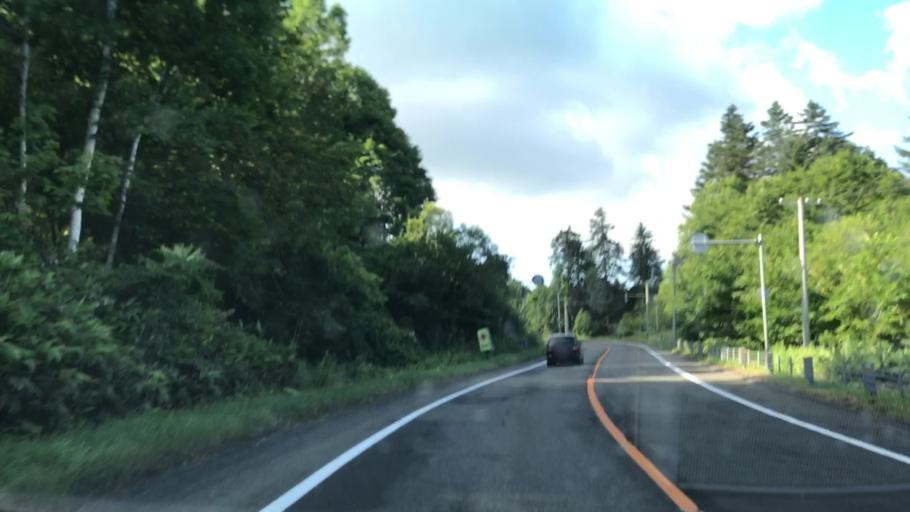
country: JP
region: Hokkaido
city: Shimo-furano
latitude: 42.9109
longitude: 142.4111
